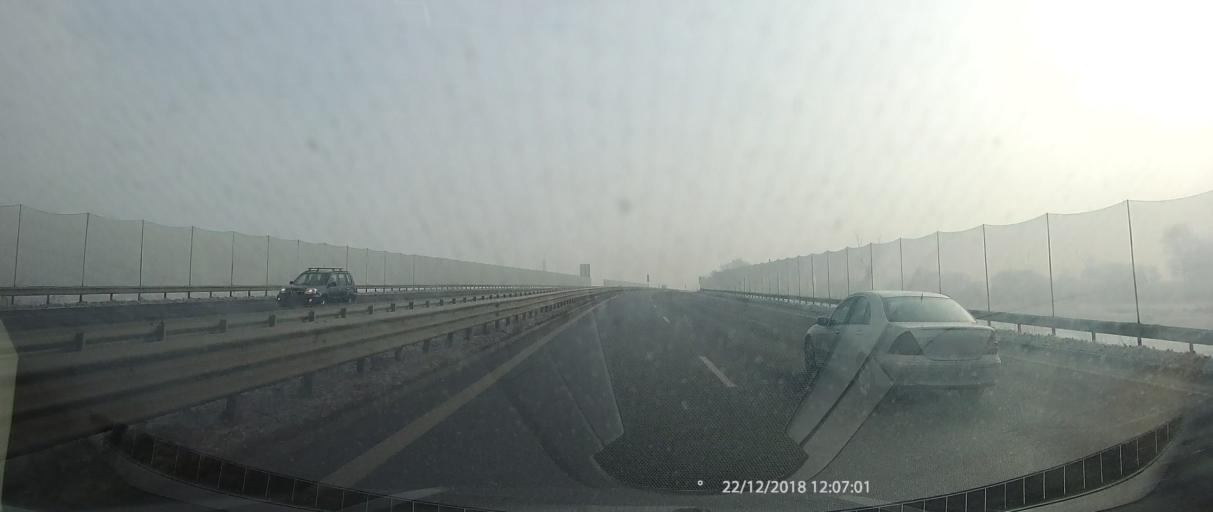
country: BG
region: Sofia-Capital
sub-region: Stolichna Obshtina
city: Sofia
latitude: 42.7501
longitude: 23.3556
